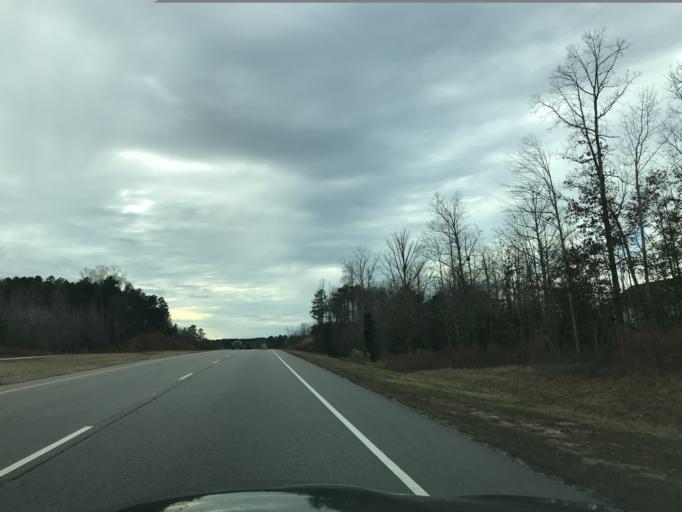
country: US
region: North Carolina
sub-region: Wake County
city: Rolesville
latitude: 35.9026
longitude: -78.4646
